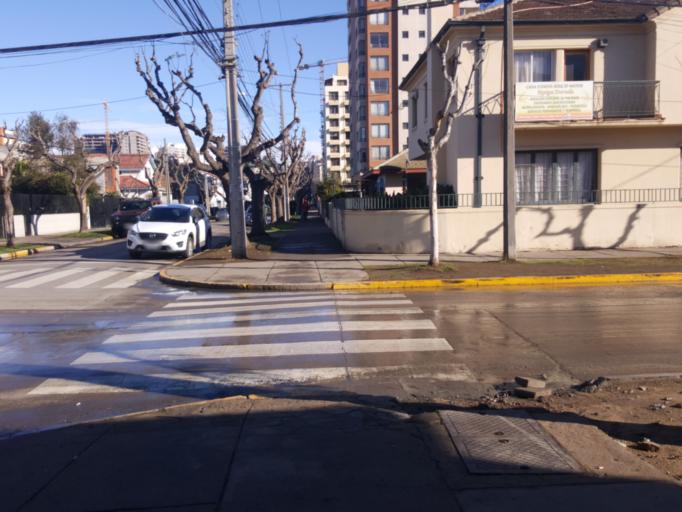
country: CL
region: Valparaiso
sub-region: Provincia de Valparaiso
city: Vina del Mar
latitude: -33.0136
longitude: -71.5468
